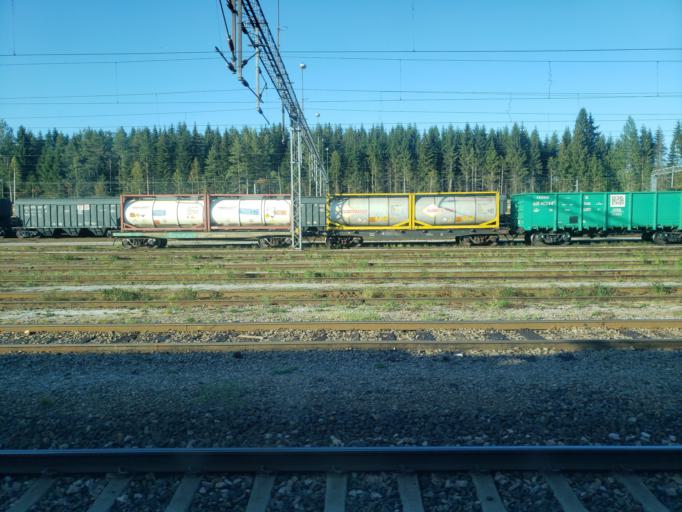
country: FI
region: South Karelia
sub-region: Lappeenranta
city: Lappeenranta
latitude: 60.8616
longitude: 28.3134
